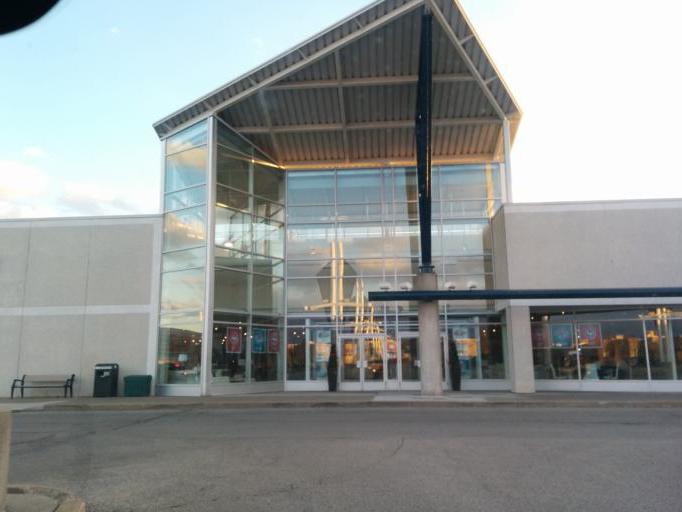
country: CA
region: Ontario
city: Oakville
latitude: 43.5144
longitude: -79.6938
